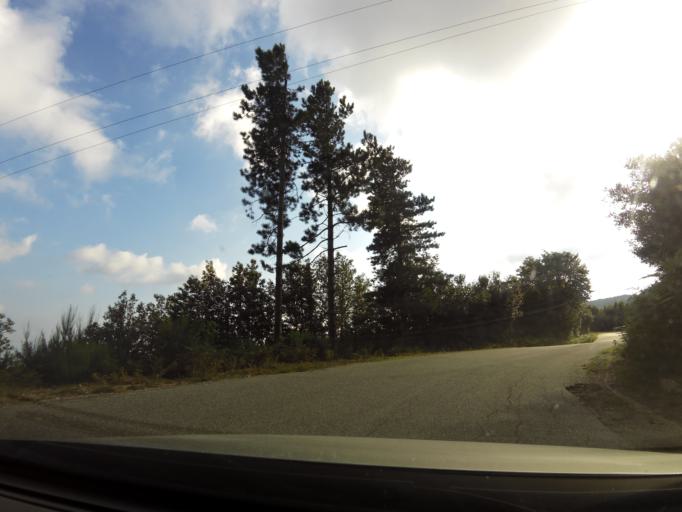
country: IT
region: Calabria
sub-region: Provincia di Vibo-Valentia
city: Nardodipace
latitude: 38.4759
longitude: 16.3882
